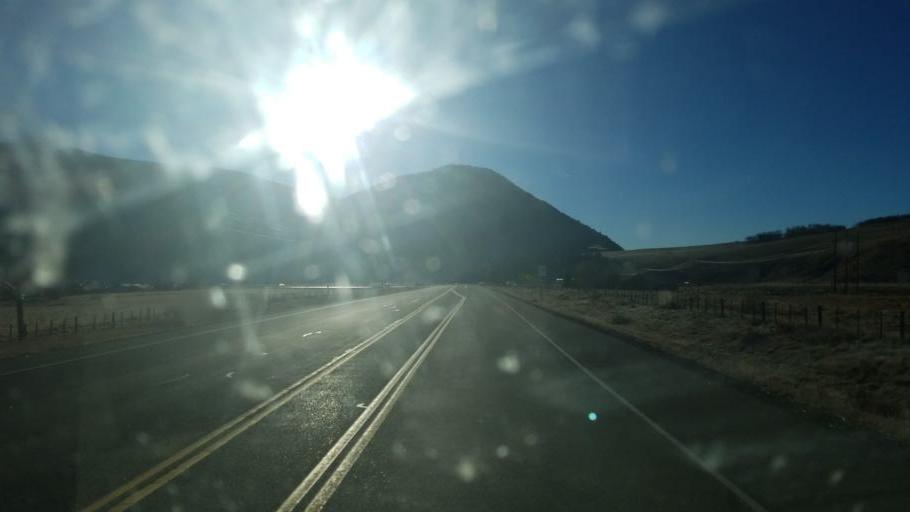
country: US
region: Colorado
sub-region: Gunnison County
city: Crested Butte
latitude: 38.8063
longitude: -106.8935
